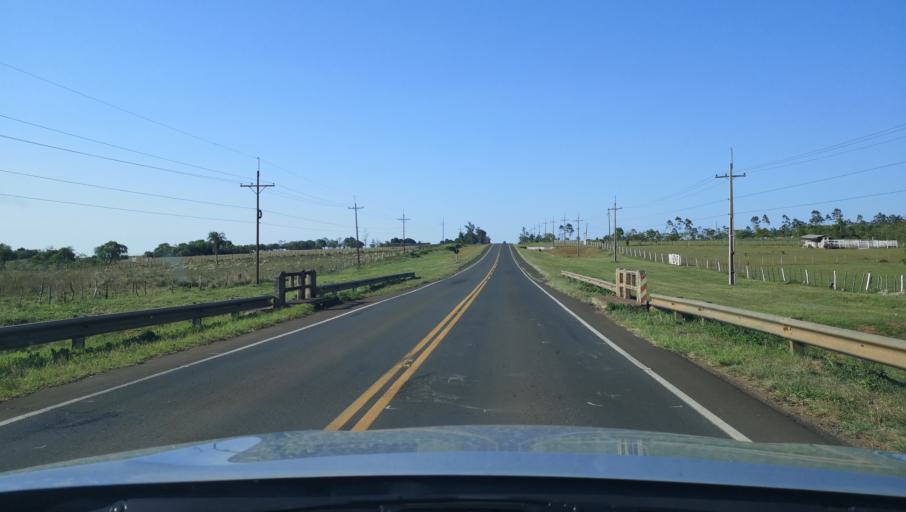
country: PY
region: Misiones
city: Santa Maria
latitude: -26.8304
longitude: -57.0311
